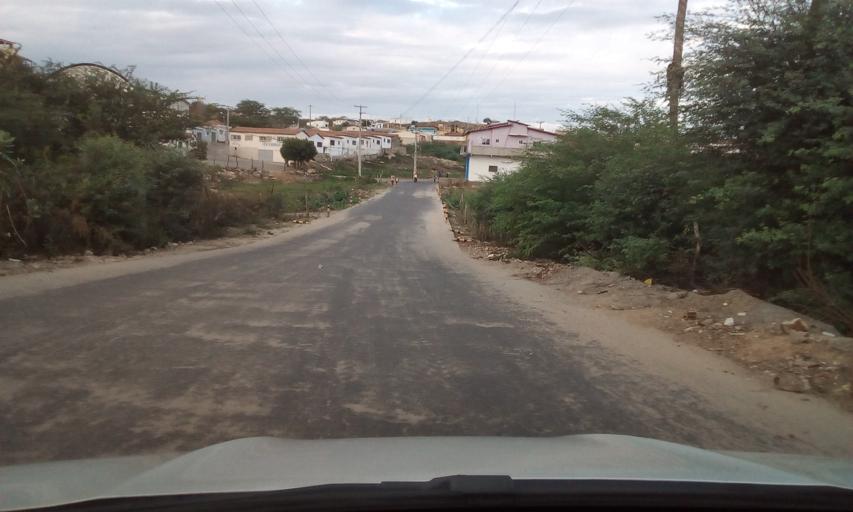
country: BR
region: Paraiba
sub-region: Picui
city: Picui
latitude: -6.5105
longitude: -36.3444
